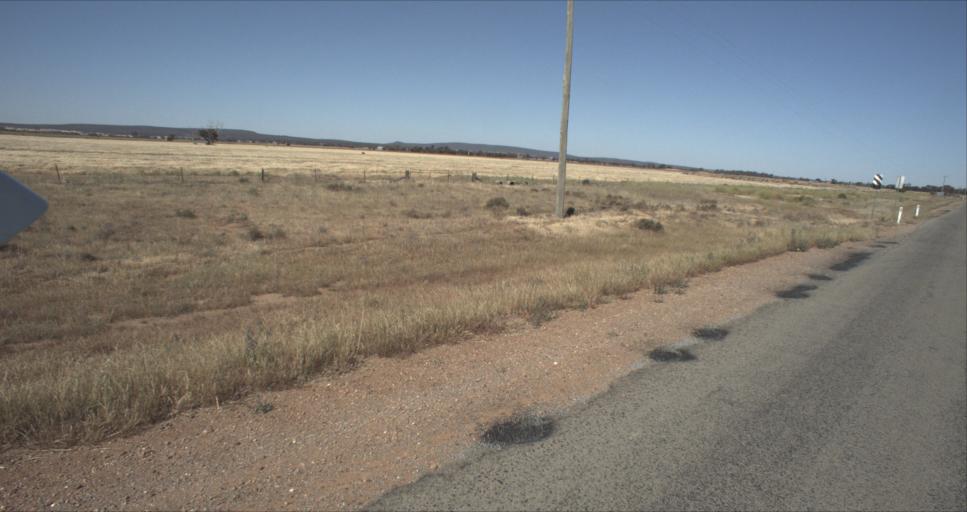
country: AU
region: New South Wales
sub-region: Leeton
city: Leeton
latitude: -34.4897
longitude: 146.3817
